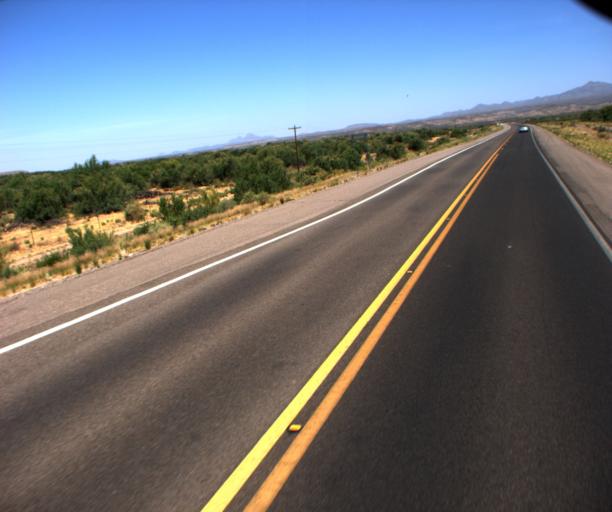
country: US
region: Arizona
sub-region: Graham County
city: Bylas
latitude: 33.1578
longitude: -110.1307
